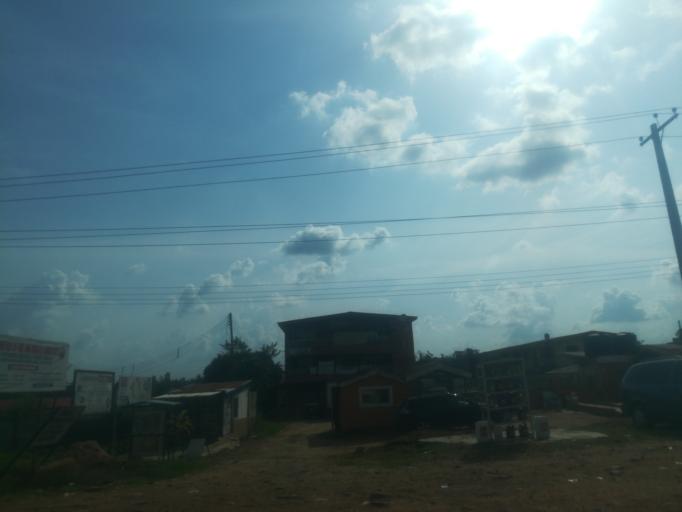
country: NG
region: Oyo
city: Ido
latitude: 7.3943
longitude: 3.8116
